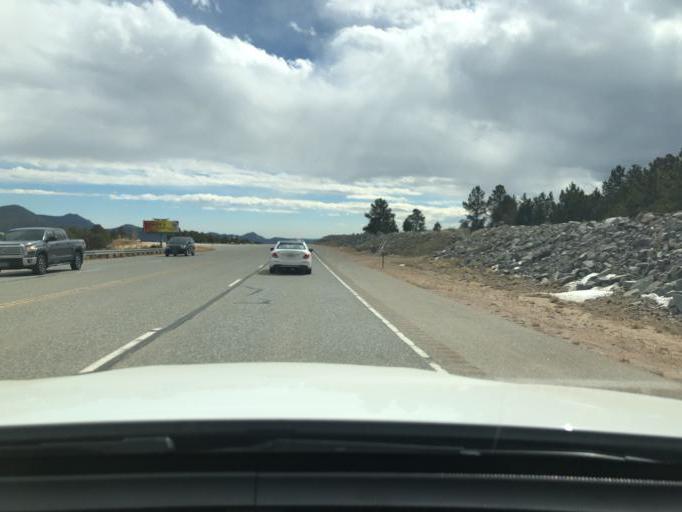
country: US
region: Colorado
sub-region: Gilpin County
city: Central City
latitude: 39.7898
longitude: -105.5061
